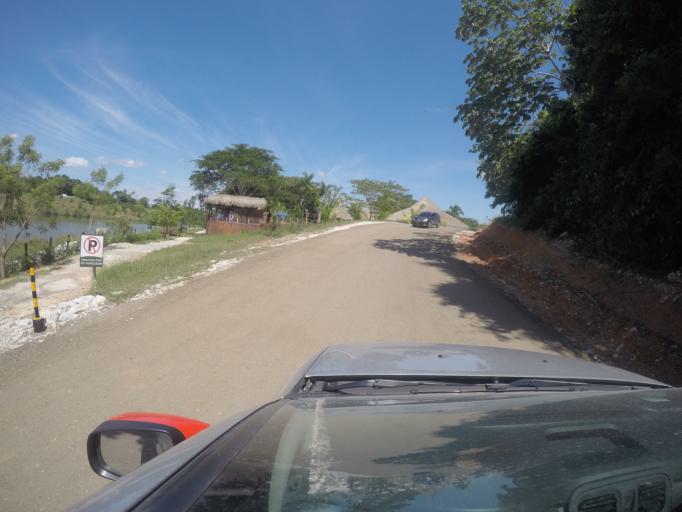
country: CO
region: Antioquia
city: Puerto Triunfo
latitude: 5.9147
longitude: -74.7228
